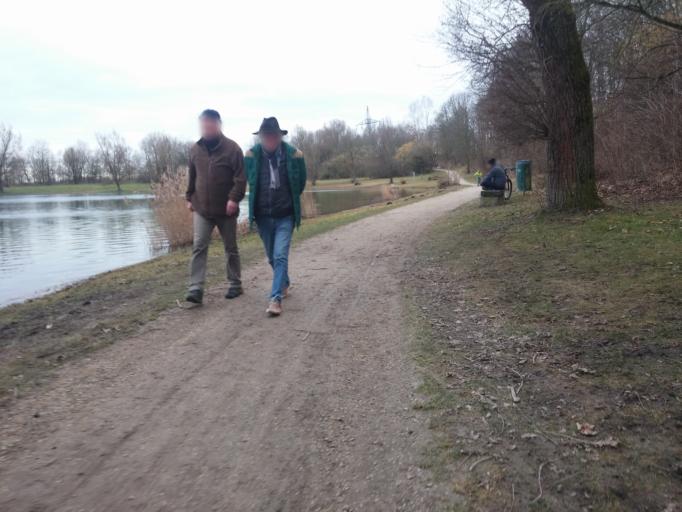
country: DE
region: Bavaria
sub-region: Upper Bavaria
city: Unterfoehring
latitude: 48.1940
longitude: 11.6671
